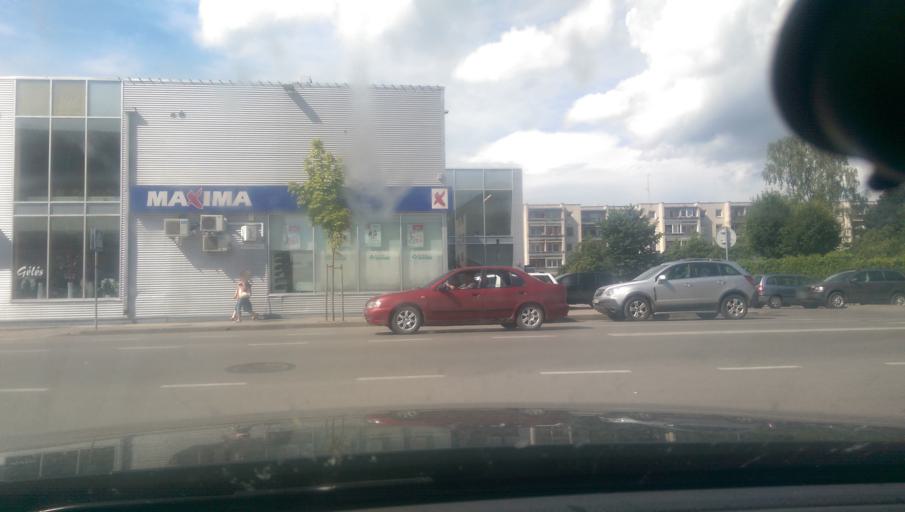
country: LT
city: Prienai
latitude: 54.6376
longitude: 23.9511
